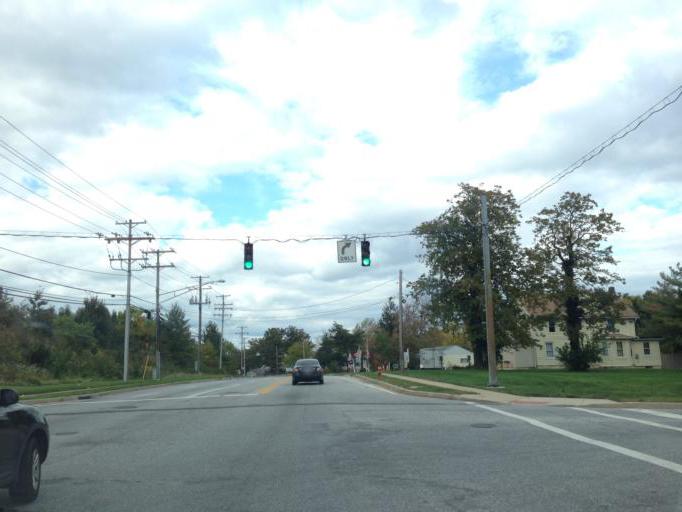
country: US
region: Maryland
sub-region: Baltimore County
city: Milford Mill
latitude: 39.3336
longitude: -76.7596
